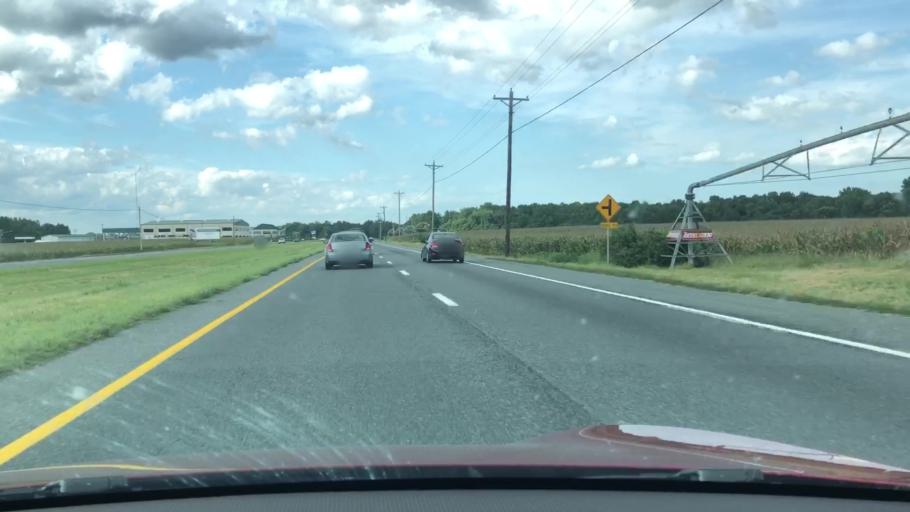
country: US
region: Delaware
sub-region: Sussex County
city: Bridgeville
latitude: 38.7858
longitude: -75.5910
